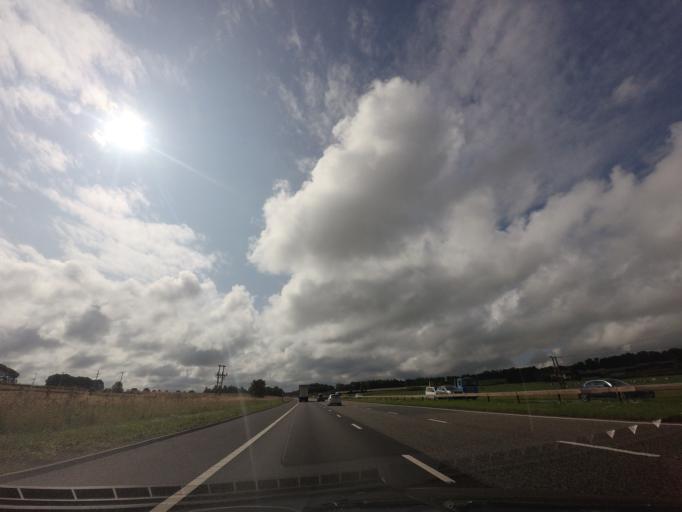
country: GB
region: England
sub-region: Cumbria
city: Penrith
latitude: 54.6184
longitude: -2.7195
